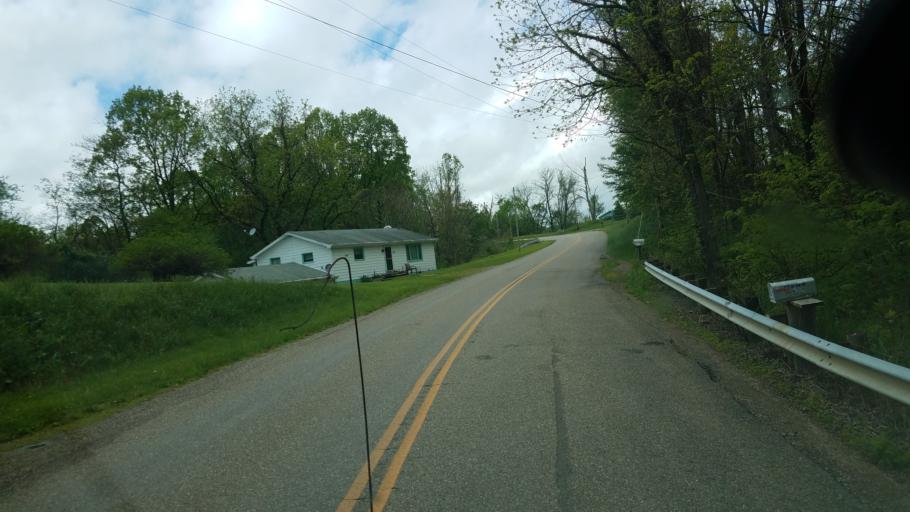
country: US
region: Ohio
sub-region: Tuscarawas County
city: Rockford
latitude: 40.4704
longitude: -81.3054
